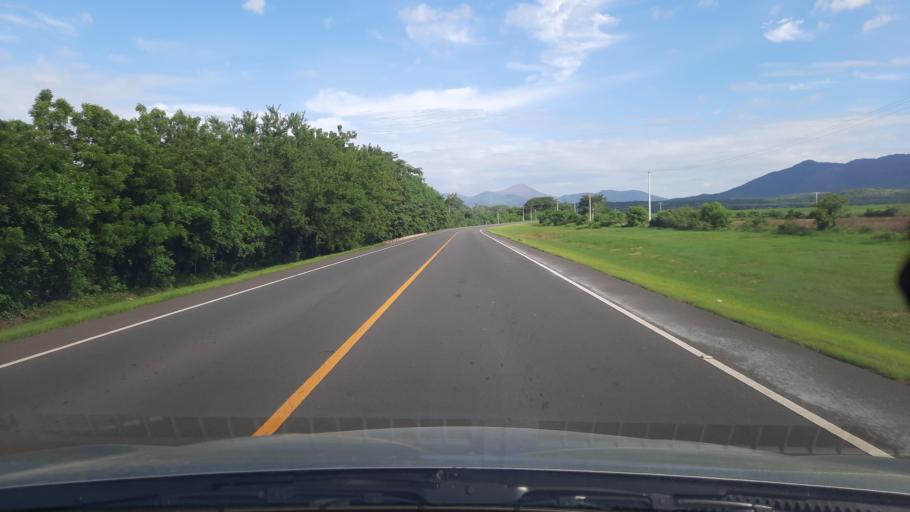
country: NI
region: Chinandega
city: Chichigalpa
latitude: 12.7604
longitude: -86.8989
